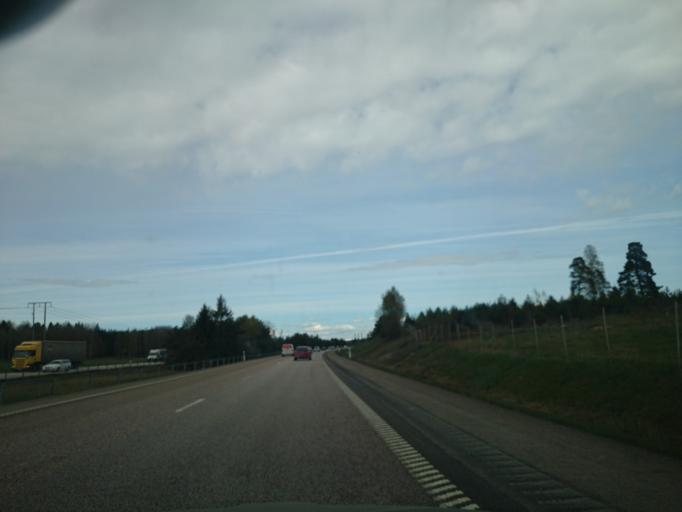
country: SE
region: Stockholm
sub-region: Sigtuna Kommun
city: Marsta
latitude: 59.6789
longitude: 17.8698
